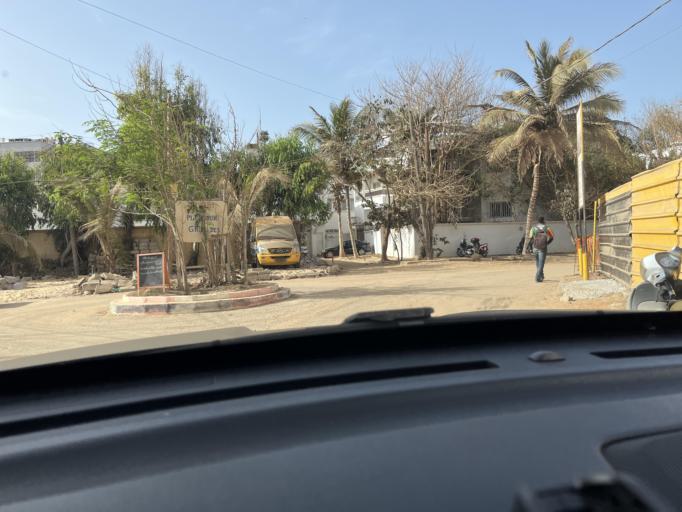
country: SN
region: Dakar
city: Mermoz Boabab
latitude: 14.7460
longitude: -17.5202
